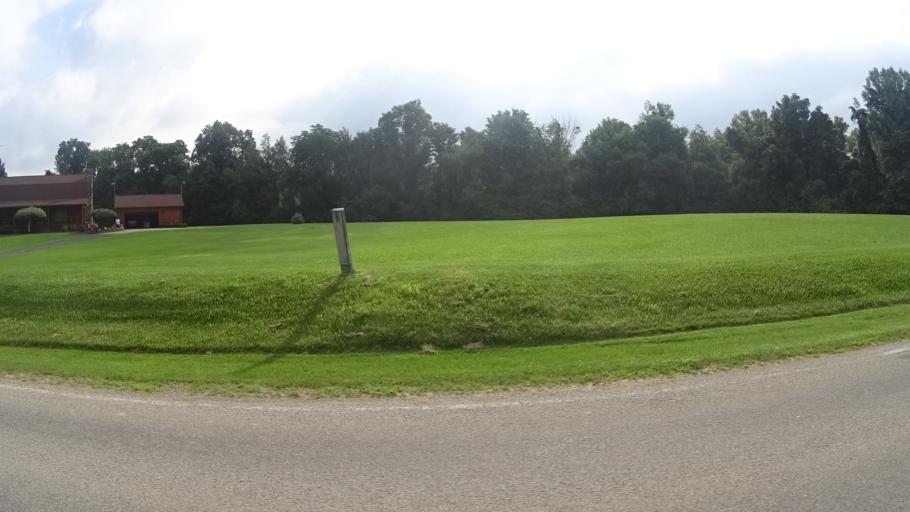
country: US
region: Ohio
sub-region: Erie County
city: Huron
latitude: 41.3379
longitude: -82.5086
